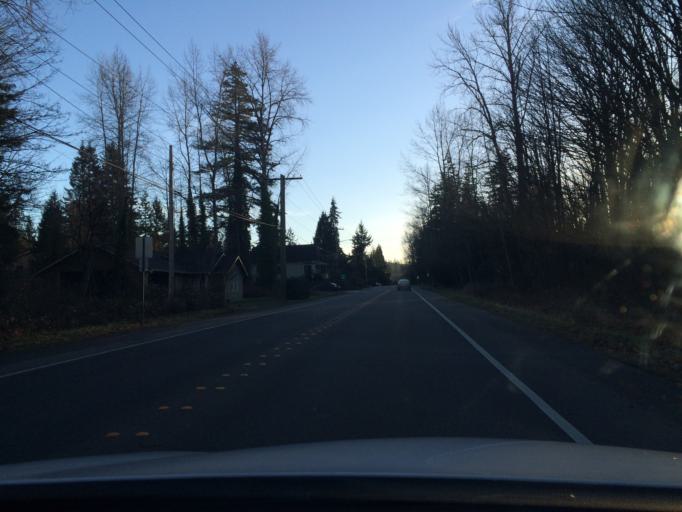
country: US
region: Washington
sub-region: Whatcom County
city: Geneva
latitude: 48.7572
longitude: -122.4215
